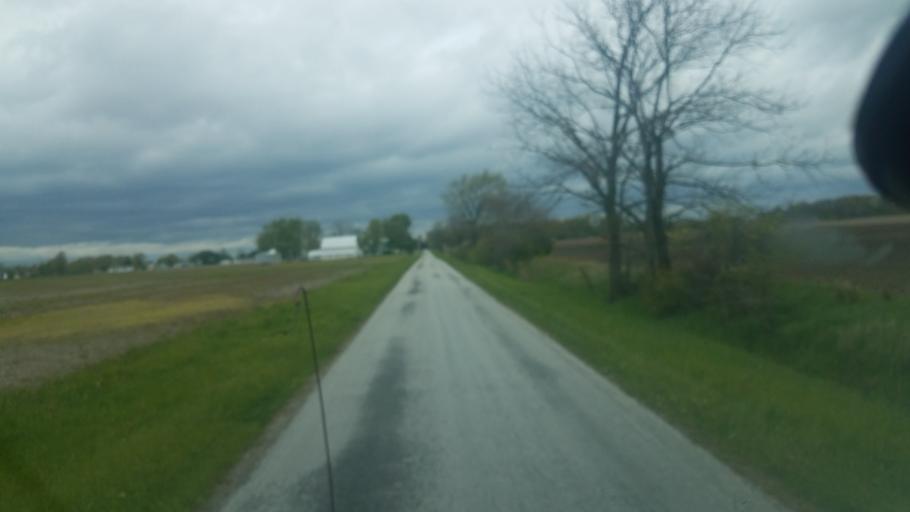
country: US
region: Ohio
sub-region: Marion County
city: Prospect
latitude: 40.5115
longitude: -83.2383
